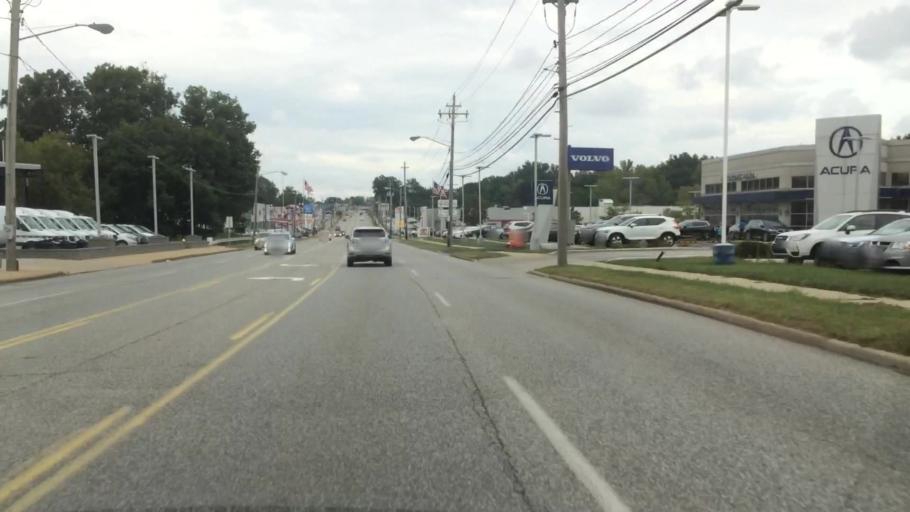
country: US
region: Ohio
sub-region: Cuyahoga County
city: Glendale
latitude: 41.4044
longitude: -81.5539
